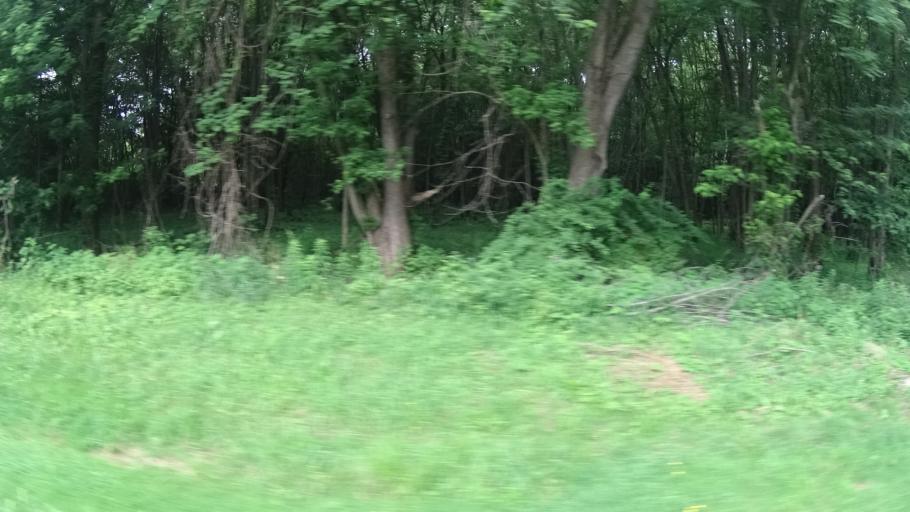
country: US
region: Ohio
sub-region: Huron County
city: Wakeman
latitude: 41.3069
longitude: -82.4812
